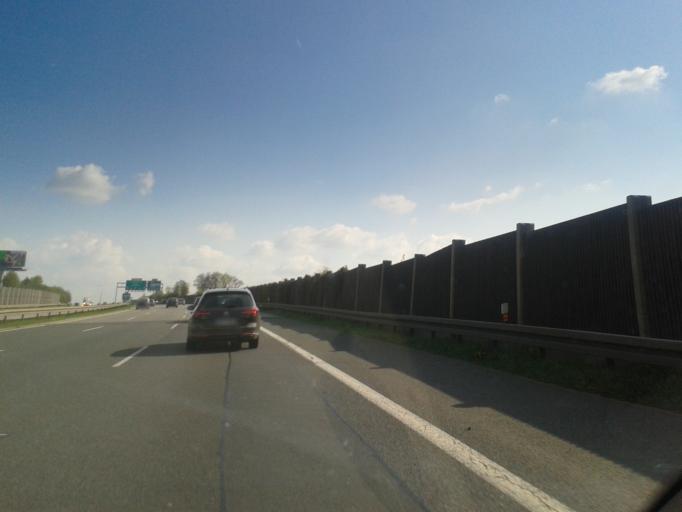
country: CZ
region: Central Bohemia
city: Hostivice
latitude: 50.0612
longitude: 14.2767
